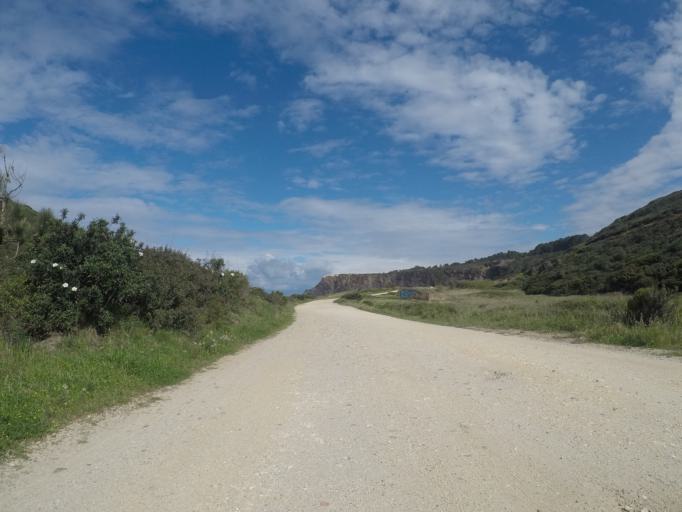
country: PT
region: Beja
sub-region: Odemira
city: Sao Teotonio
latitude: 37.4391
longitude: -8.7946
